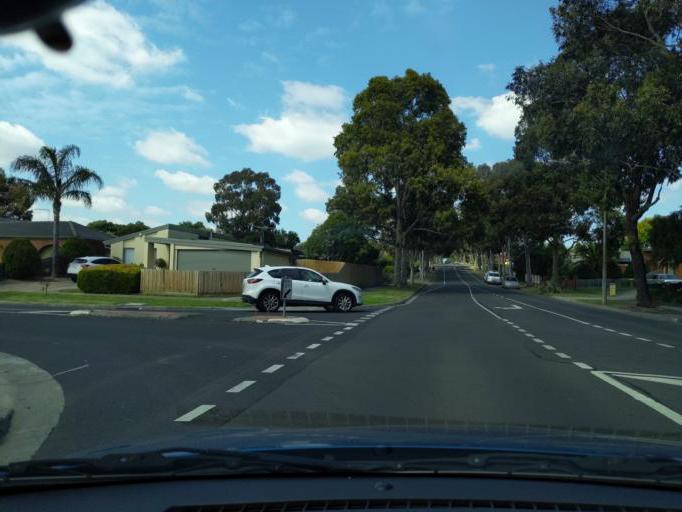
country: AU
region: Victoria
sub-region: Knox
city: Scoresby
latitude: -37.9162
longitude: 145.2462
